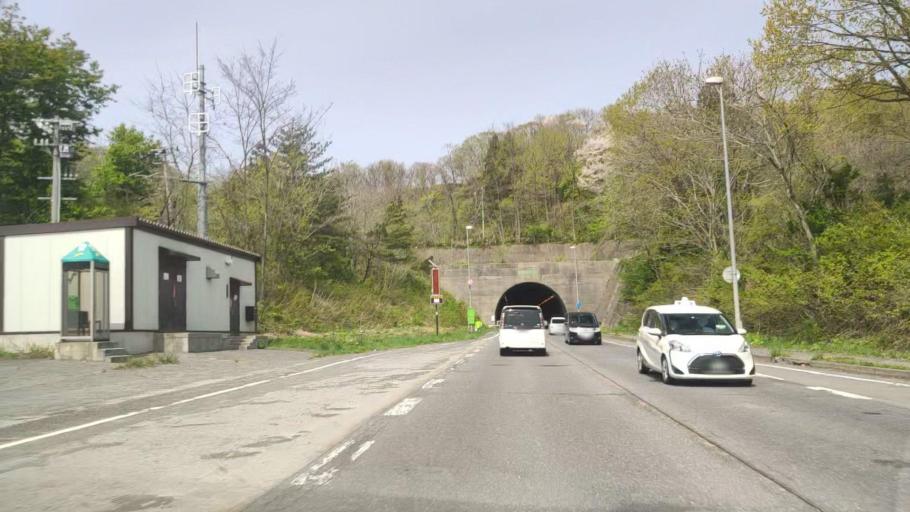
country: JP
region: Aomori
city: Aomori Shi
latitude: 40.8553
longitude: 140.8397
